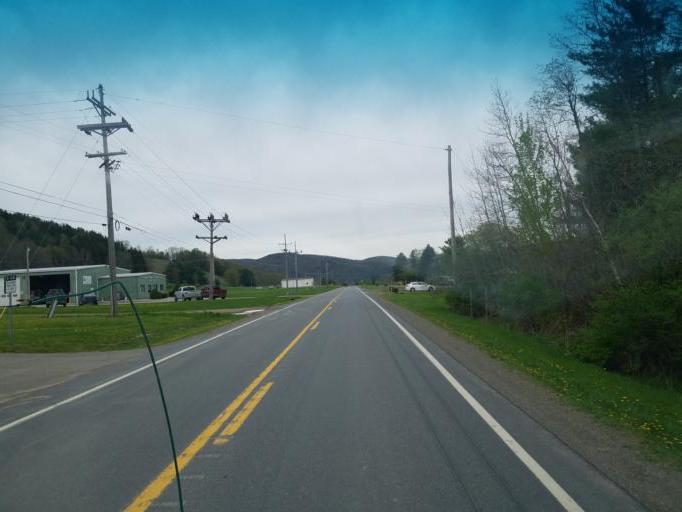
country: US
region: Pennsylvania
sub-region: Tioga County
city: Westfield
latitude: 41.8968
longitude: -77.5328
